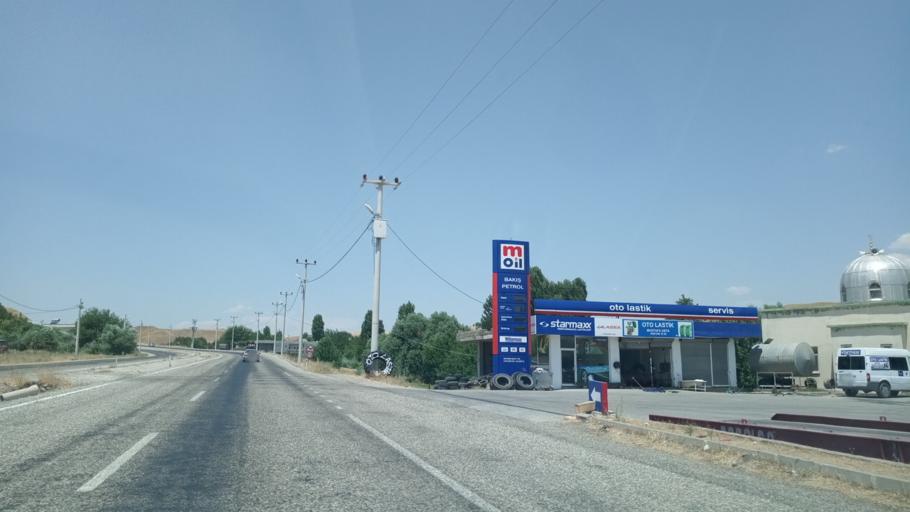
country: TR
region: Batman
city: Bekirhan
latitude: 38.1436
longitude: 41.2879
